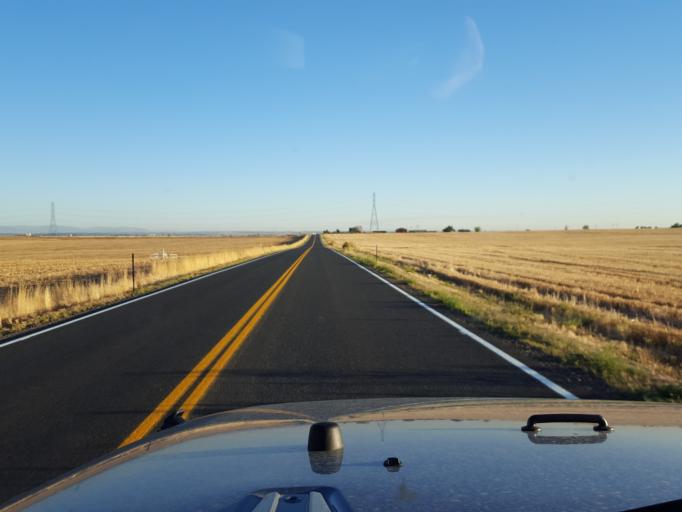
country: US
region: Colorado
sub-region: Boulder County
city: Erie
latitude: 40.0522
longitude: -105.0182
